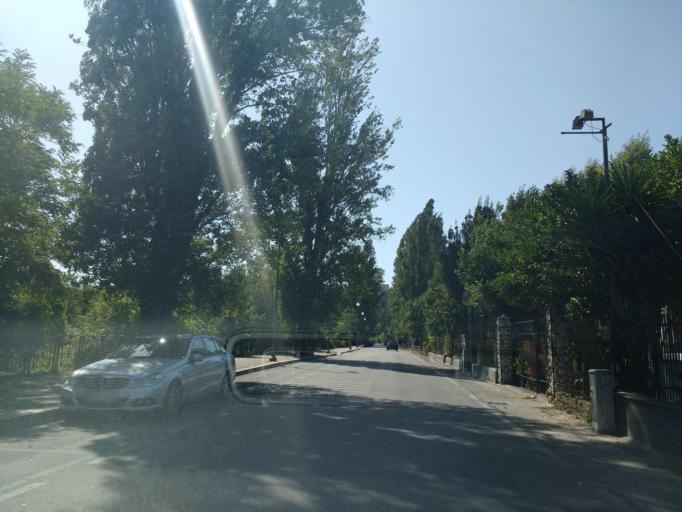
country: IT
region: Latium
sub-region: Citta metropolitana di Roma Capitale
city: Castel Gandolfo
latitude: 41.7611
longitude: 12.6622
